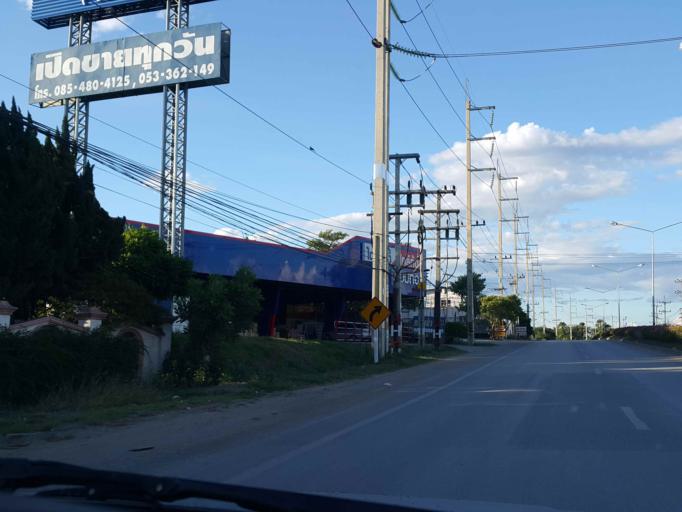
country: TH
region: Chiang Mai
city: Chom Thong
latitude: 18.4386
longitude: 98.6888
